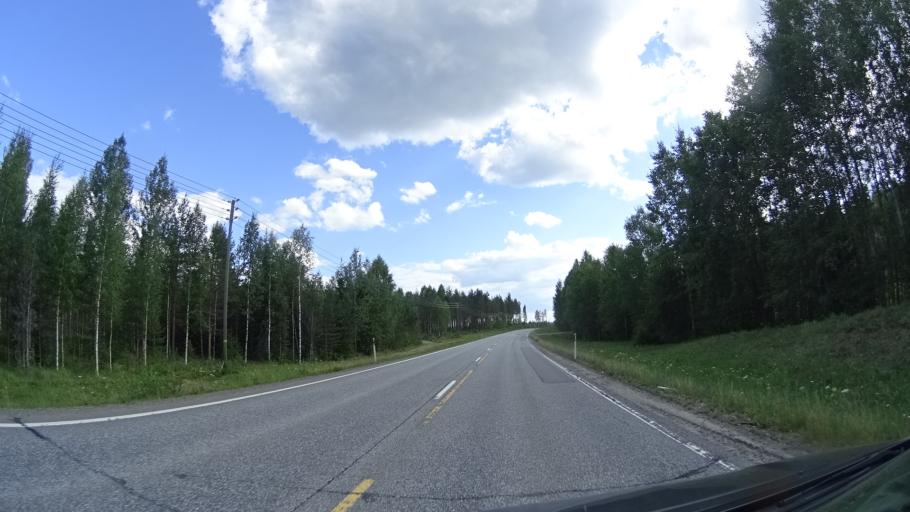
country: FI
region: Southern Savonia
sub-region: Savonlinna
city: Punkaharju
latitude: 61.6746
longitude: 29.4136
